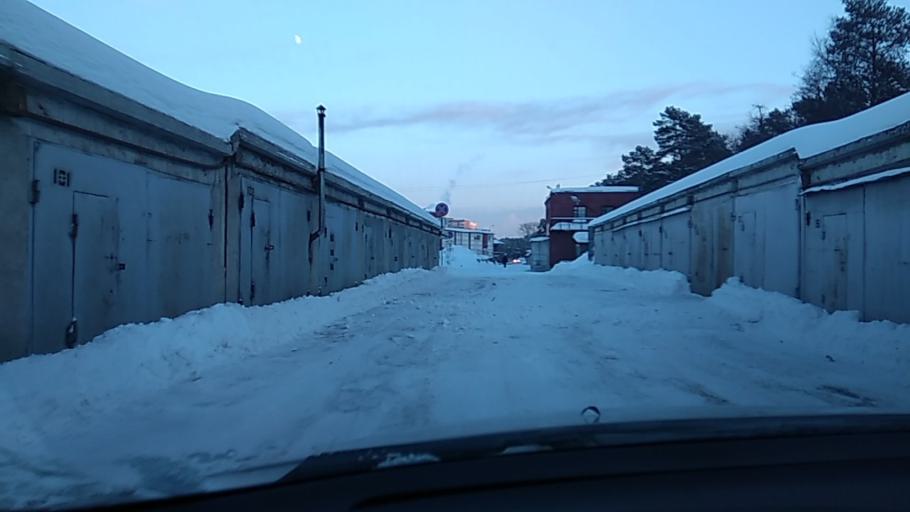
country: RU
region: Sverdlovsk
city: Sovkhoznyy
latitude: 56.7926
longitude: 60.5656
